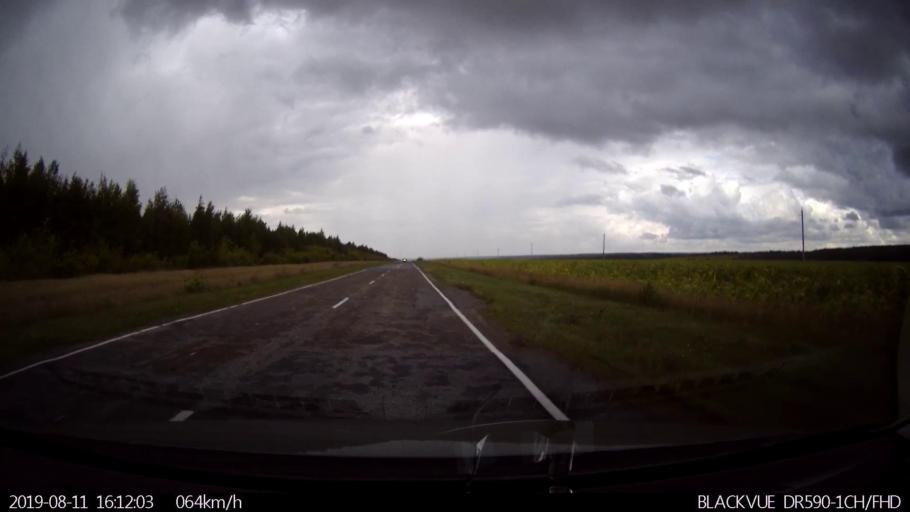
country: RU
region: Ulyanovsk
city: Ignatovka
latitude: 54.0082
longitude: 47.6417
